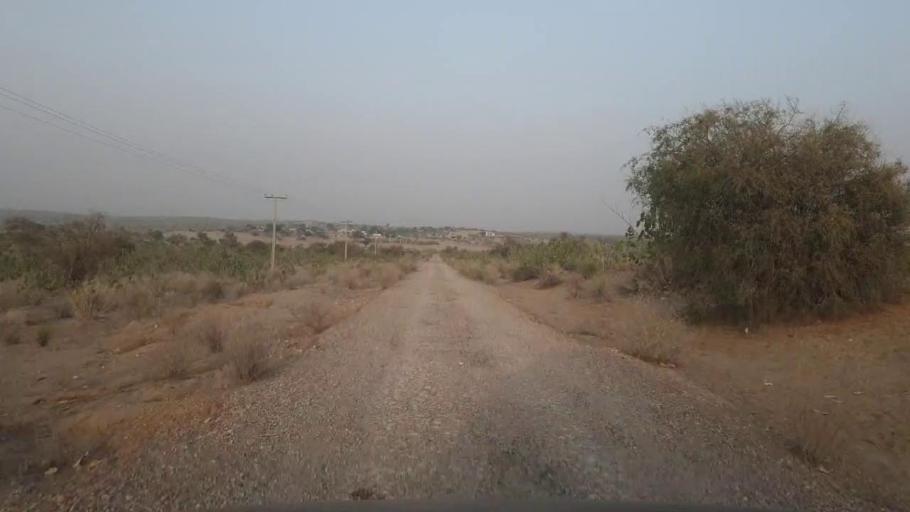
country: PK
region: Sindh
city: Chor
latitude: 25.5322
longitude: 69.9565
